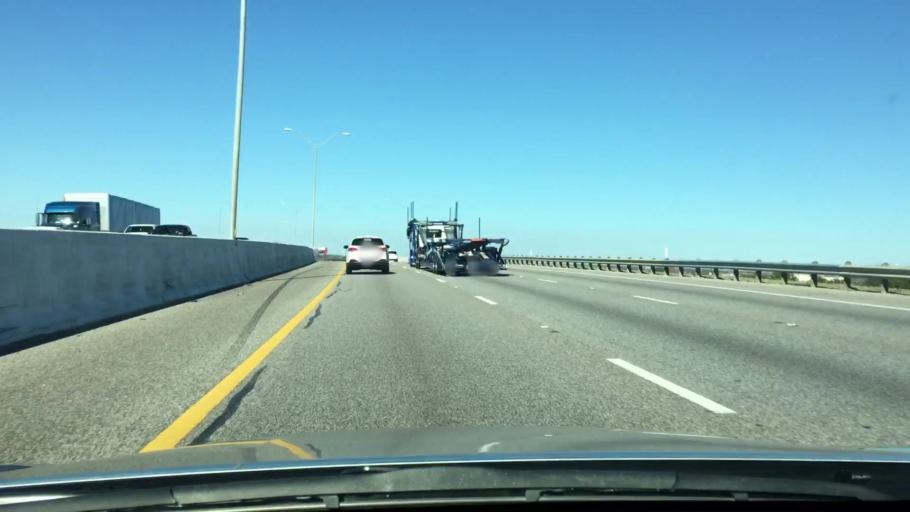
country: US
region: Texas
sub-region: Williamson County
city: Georgetown
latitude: 30.6063
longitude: -97.6864
